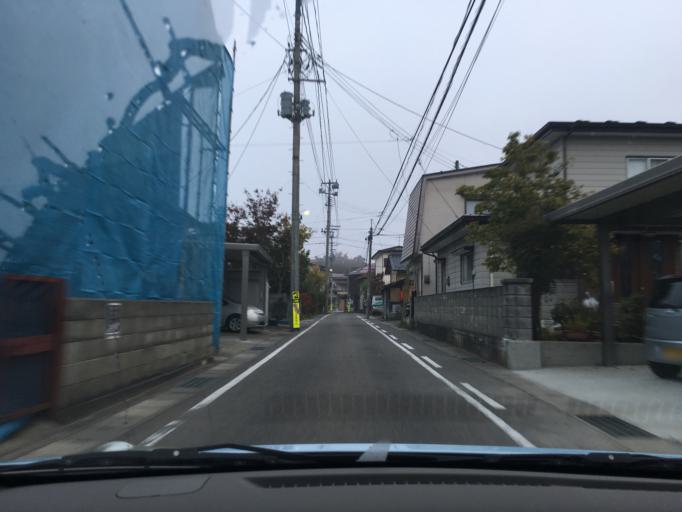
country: JP
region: Fukushima
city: Kitakata
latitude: 37.5022
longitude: 139.9387
